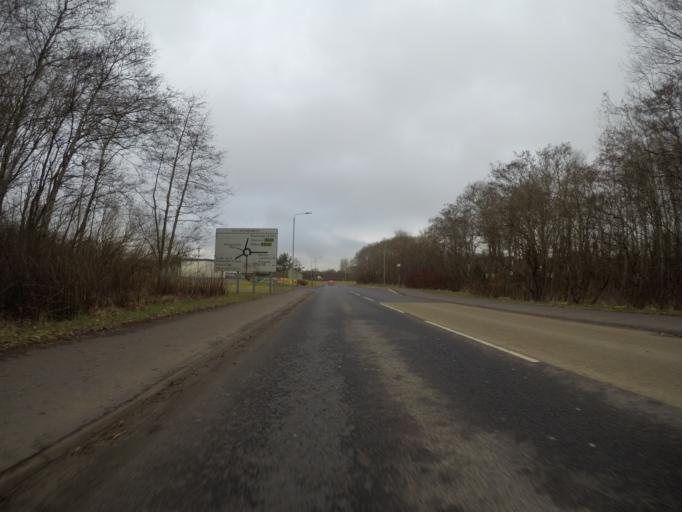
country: GB
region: Scotland
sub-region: North Ayrshire
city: Irvine
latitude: 55.6317
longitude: -4.6435
